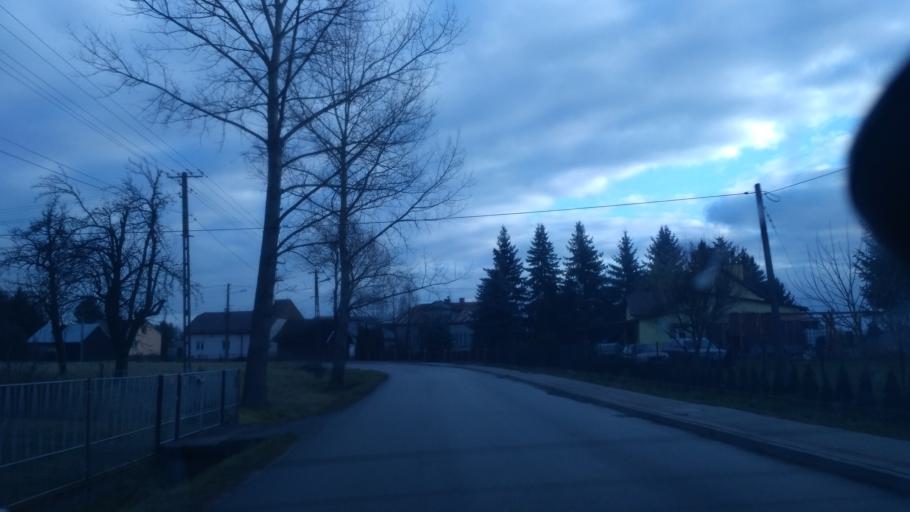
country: PL
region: Subcarpathian Voivodeship
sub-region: Powiat rzeszowski
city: Wolka Podlesna
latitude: 50.1019
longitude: 22.1454
